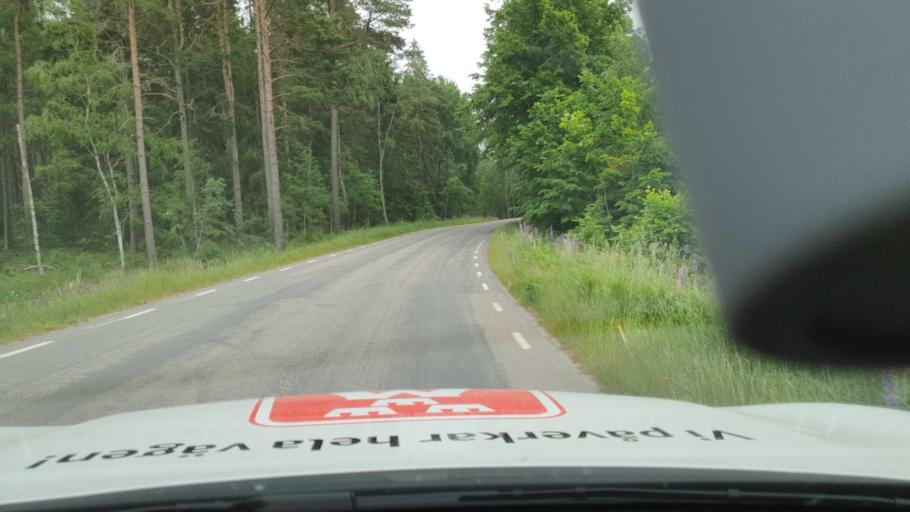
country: SE
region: Vaestra Goetaland
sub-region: Tibro Kommun
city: Tibro
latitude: 58.4160
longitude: 14.2306
